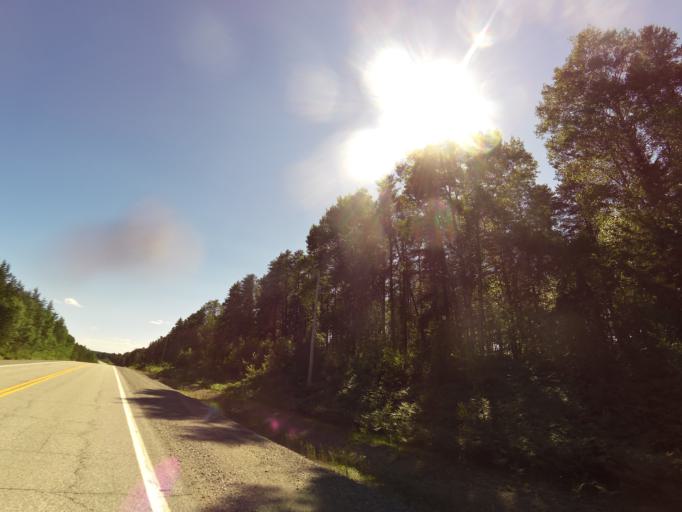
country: CA
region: Quebec
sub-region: Abitibi-Temiscamingue
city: Senneterre
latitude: 48.1139
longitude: -77.3907
